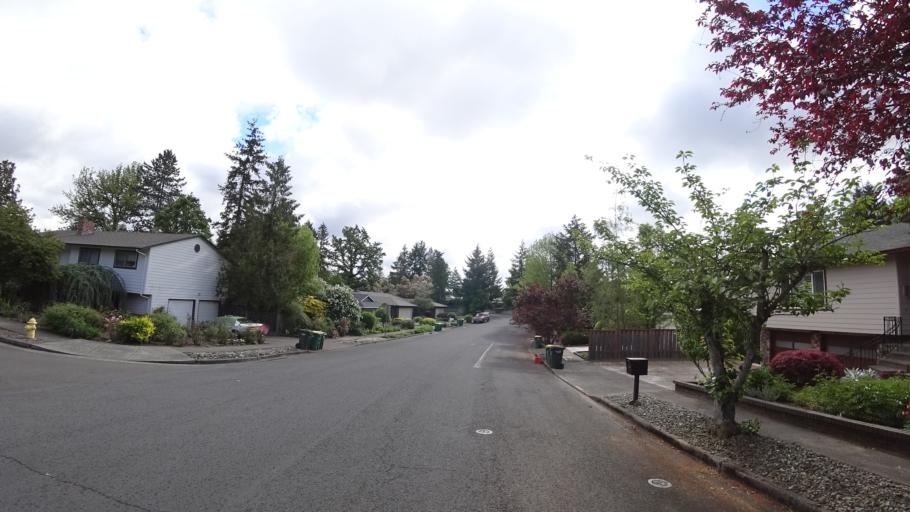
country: US
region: Oregon
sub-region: Washington County
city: Beaverton
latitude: 45.4692
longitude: -122.8210
